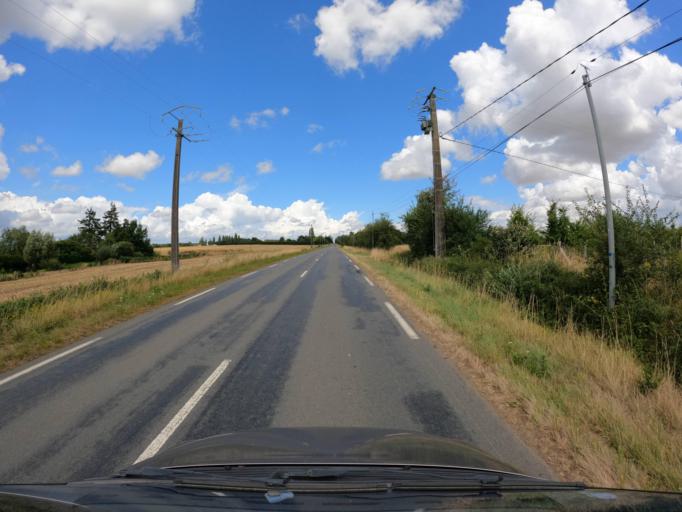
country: FR
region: Pays de la Loire
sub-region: Departement de la Sarthe
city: Juigne-sur-Sarthe
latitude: 47.8790
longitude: -0.3016
